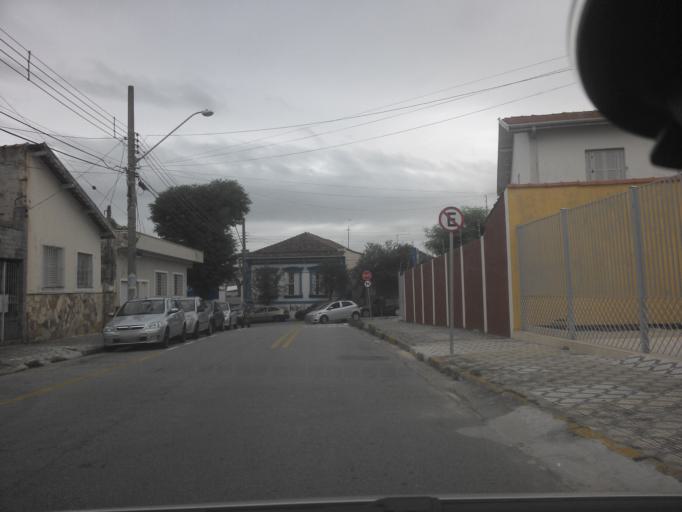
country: BR
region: Sao Paulo
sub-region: Taubate
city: Taubate
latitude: -23.0281
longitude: -45.5520
